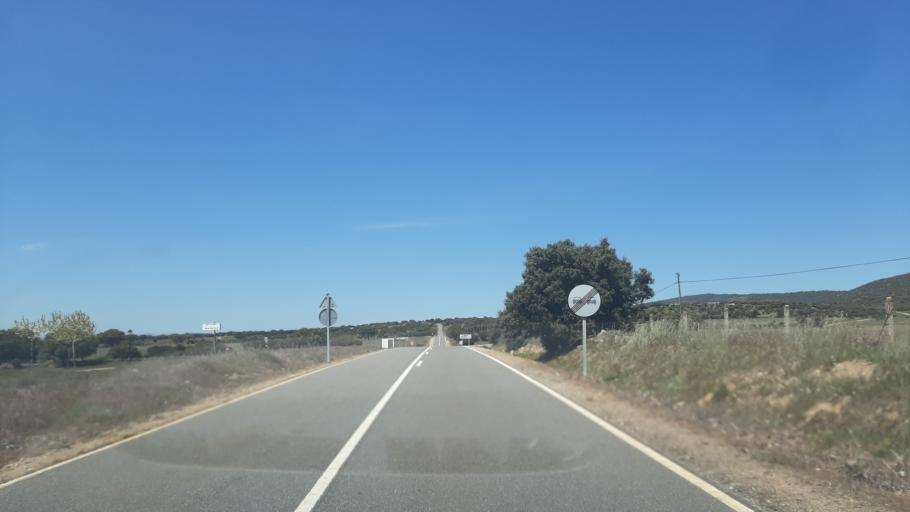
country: ES
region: Castille and Leon
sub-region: Provincia de Salamanca
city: Puente del Congosto
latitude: 40.5237
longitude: -5.5001
